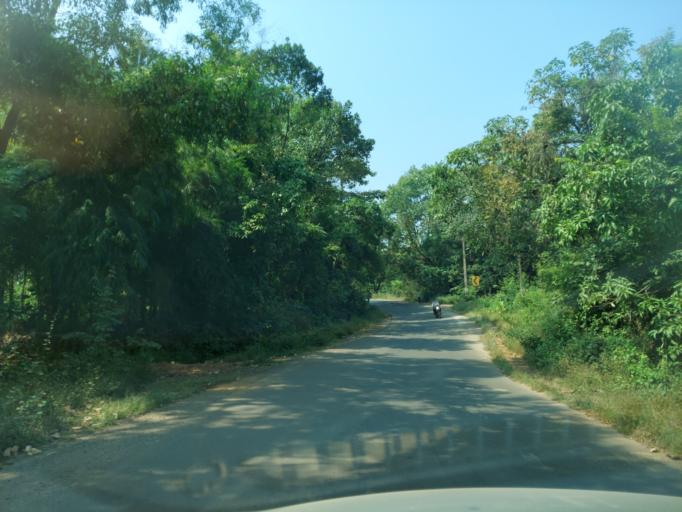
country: IN
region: Maharashtra
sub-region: Sindhudurg
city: Kudal
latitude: 15.9675
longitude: 73.5887
